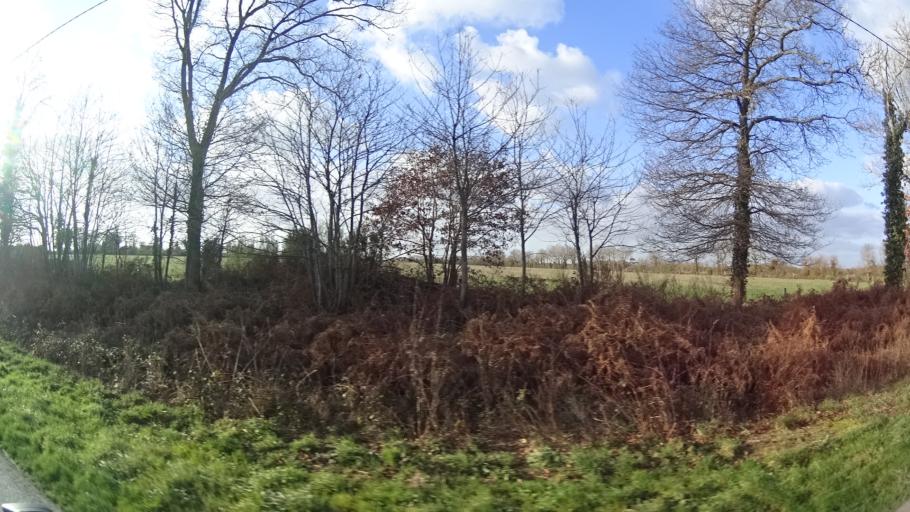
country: FR
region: Pays de la Loire
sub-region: Departement de la Loire-Atlantique
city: Plesse
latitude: 47.5835
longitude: -1.8579
